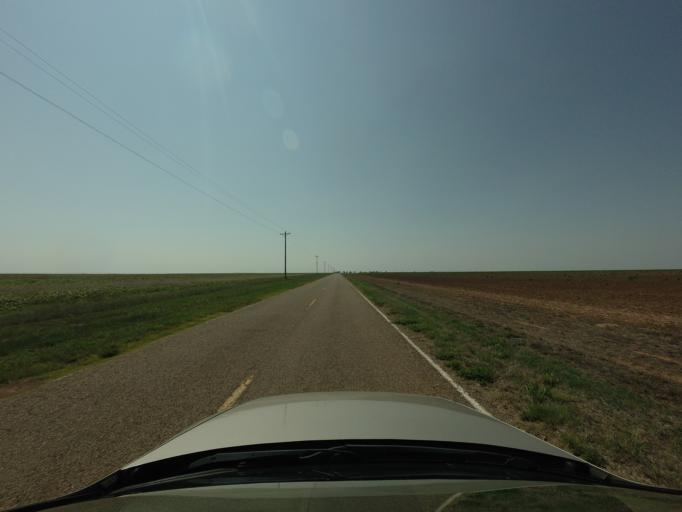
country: US
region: New Mexico
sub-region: Curry County
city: Cannon Air Force Base
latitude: 34.6275
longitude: -103.3023
